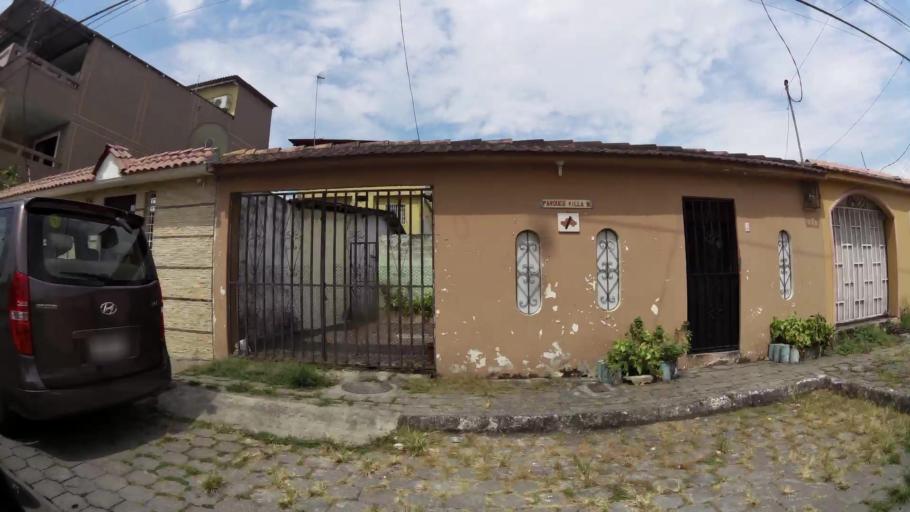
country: EC
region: Guayas
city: Eloy Alfaro
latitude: -2.1275
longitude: -79.9047
